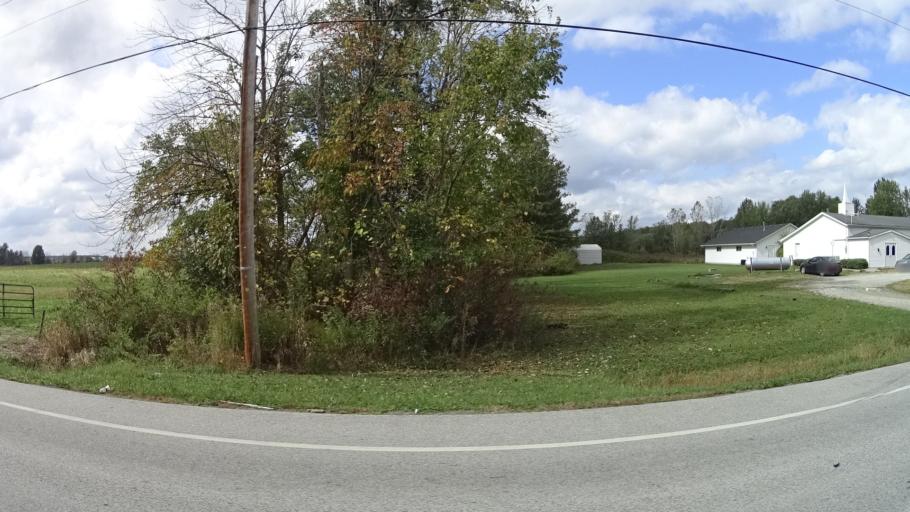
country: US
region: Ohio
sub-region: Lorain County
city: Eaton Estates
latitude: 41.3011
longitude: -82.0015
